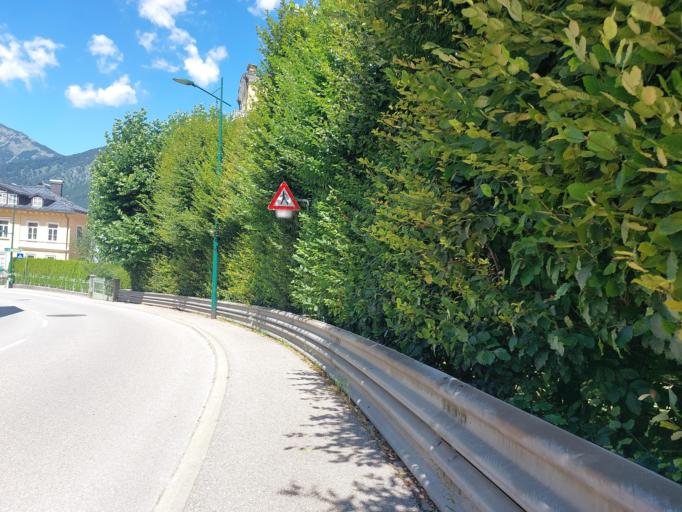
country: AT
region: Upper Austria
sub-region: Politischer Bezirk Gmunden
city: Bad Ischl
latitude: 47.7087
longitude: 13.6240
